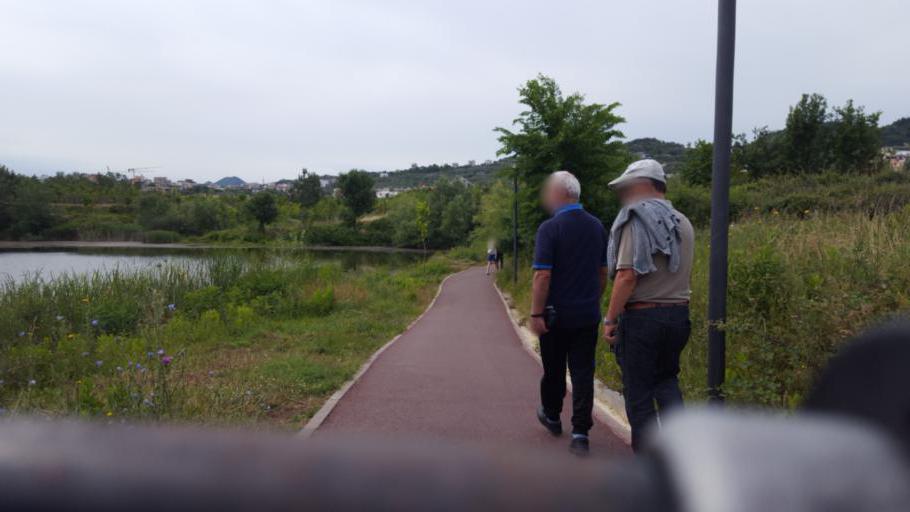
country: AL
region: Tirane
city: Tirana
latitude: 41.3075
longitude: 19.8198
